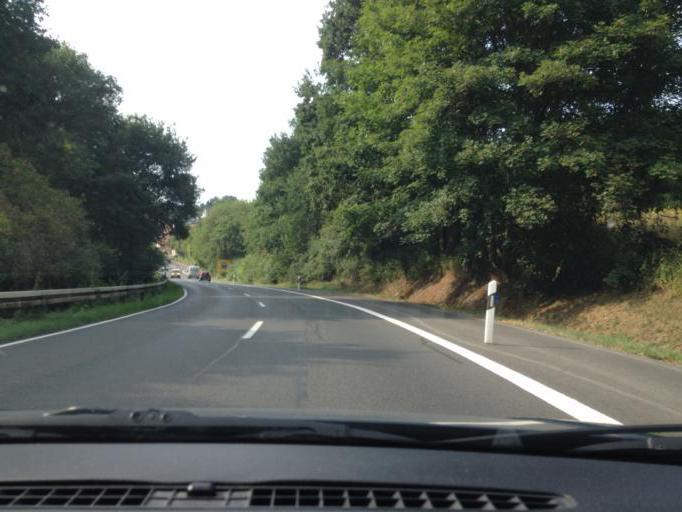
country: DE
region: Saarland
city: Namborn
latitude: 49.5066
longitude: 7.1626
